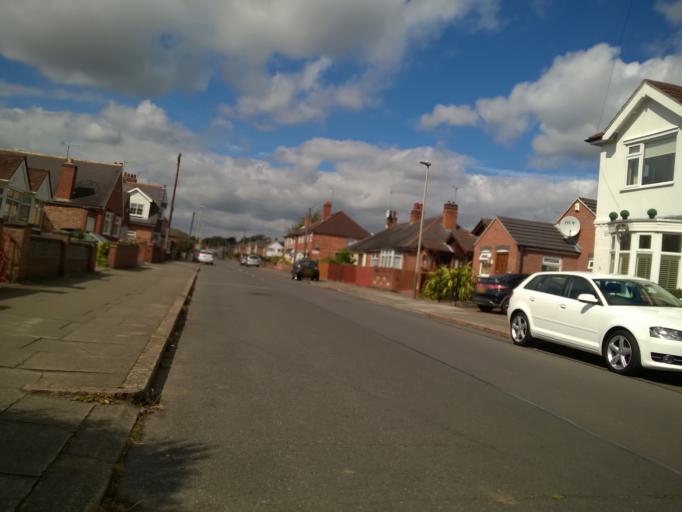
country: GB
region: England
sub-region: City of Leicester
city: Leicester
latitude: 52.6464
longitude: -1.1606
